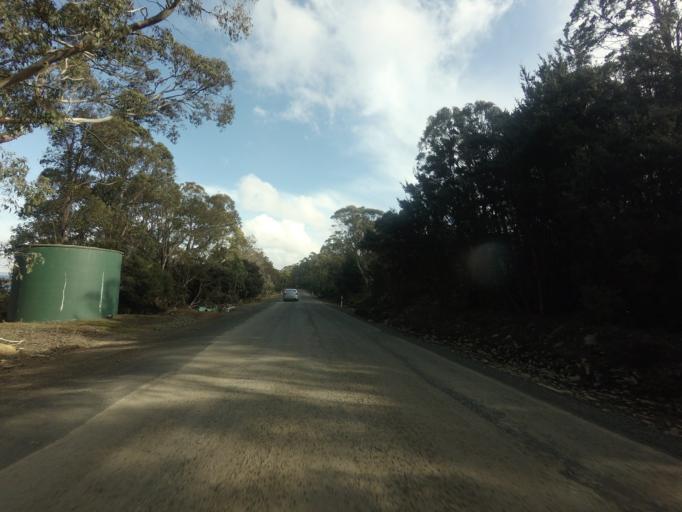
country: AU
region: Tasmania
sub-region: Meander Valley
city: Deloraine
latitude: -41.7793
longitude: 146.7085
